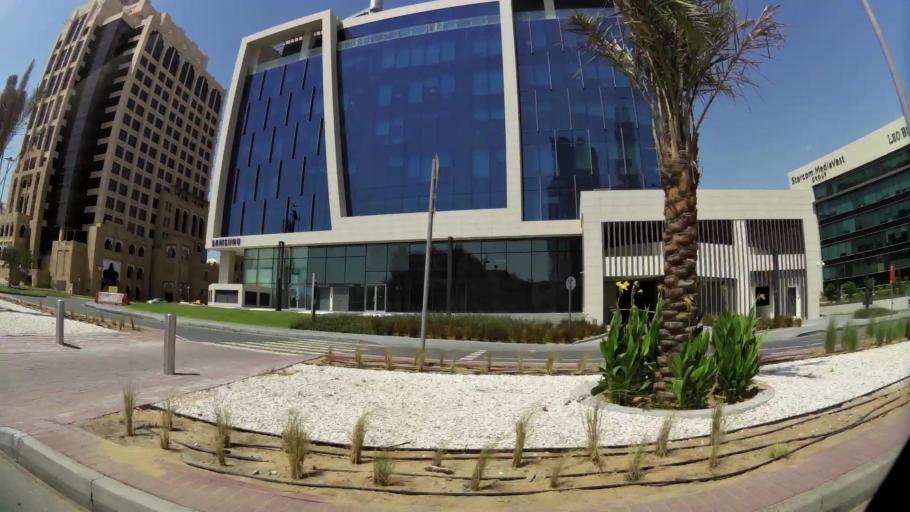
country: AE
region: Dubai
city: Dubai
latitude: 25.0940
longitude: 55.1542
